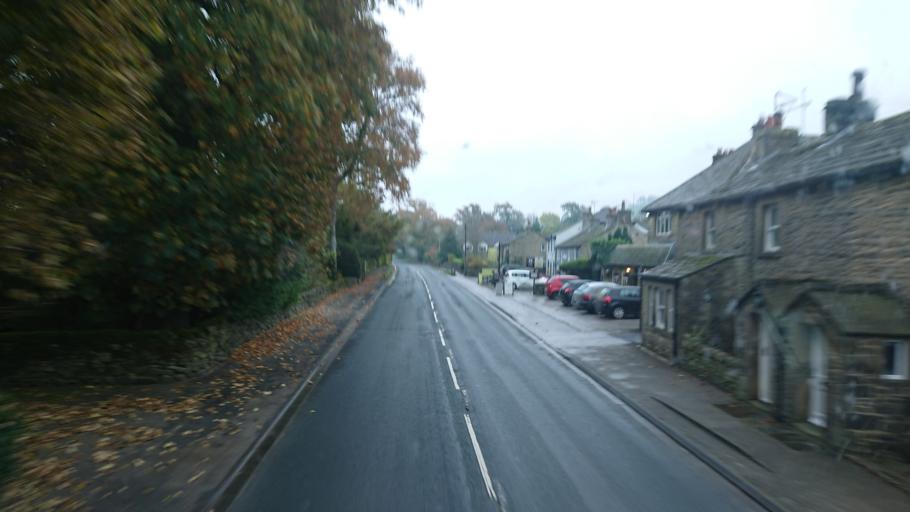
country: GB
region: England
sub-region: North Yorkshire
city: Embsay
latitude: 54.0366
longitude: -2.0363
